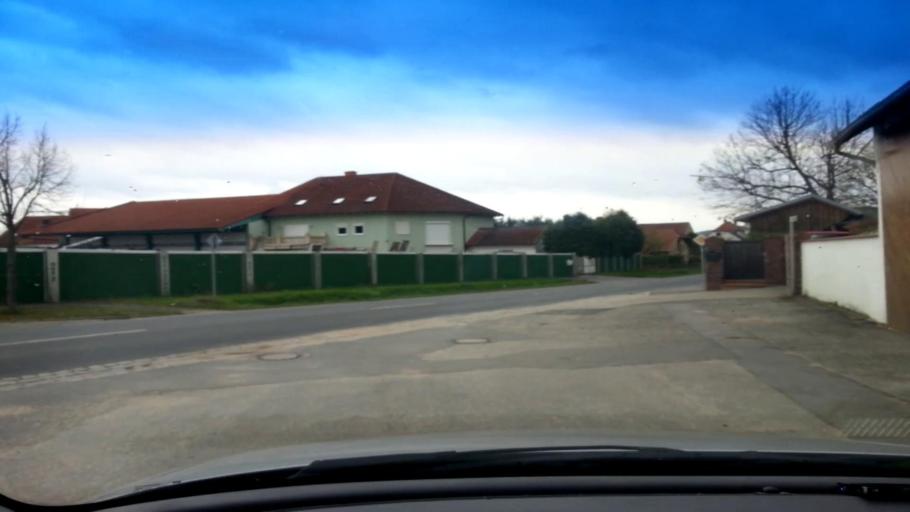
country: DE
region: Bavaria
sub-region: Regierungsbezirk Unterfranken
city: Stettfeld
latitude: 49.9696
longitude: 10.7298
